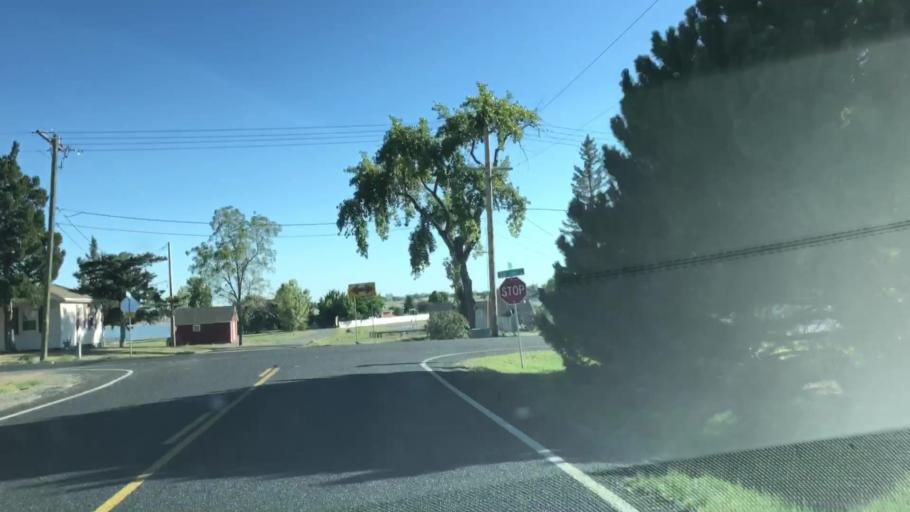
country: US
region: Colorado
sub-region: Larimer County
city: Loveland
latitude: 40.4512
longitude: -105.0583
